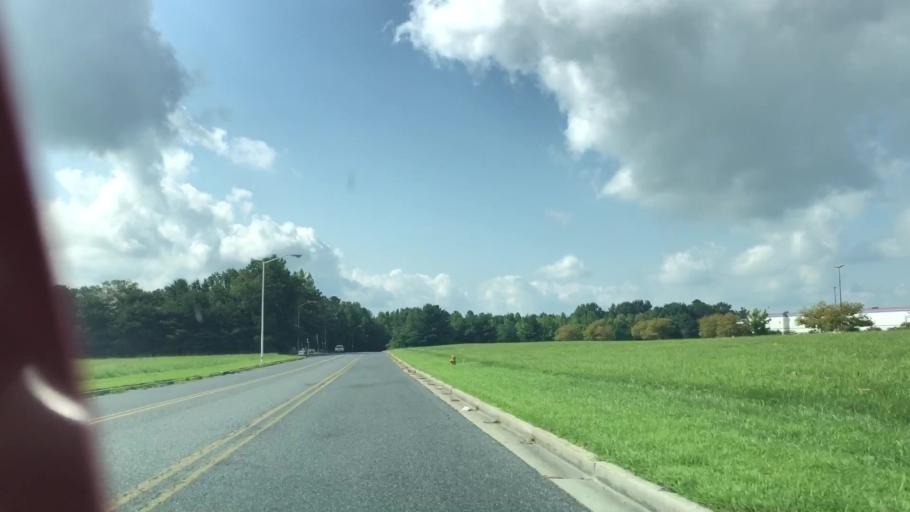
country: US
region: Maryland
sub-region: Wicomico County
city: Salisbury
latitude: 38.3993
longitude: -75.5627
